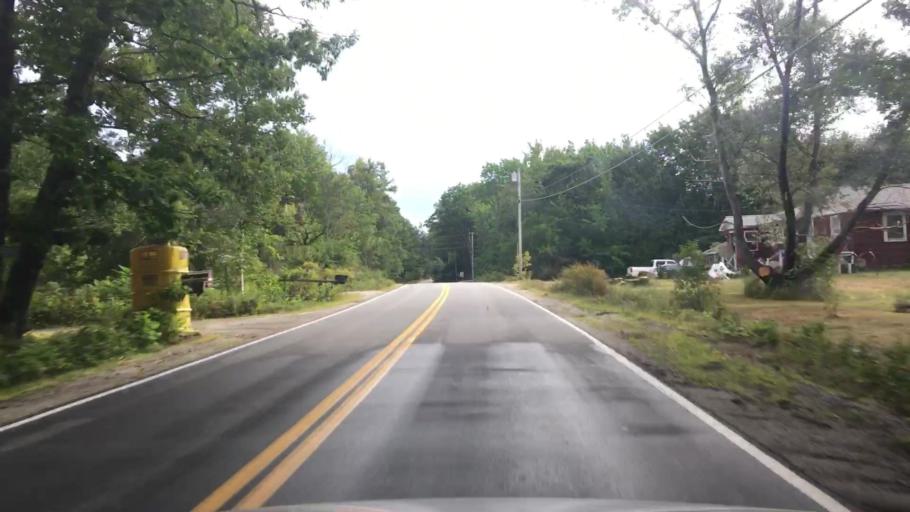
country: US
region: Maine
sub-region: Hancock County
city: Trenton
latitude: 44.4644
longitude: -68.4241
